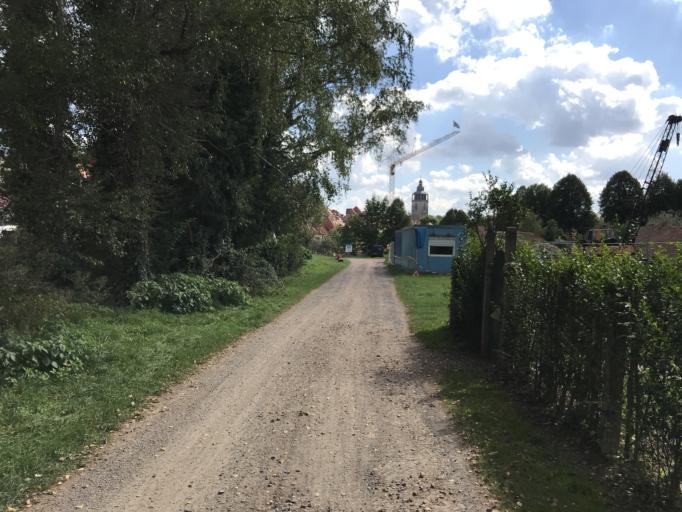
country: DE
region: Hesse
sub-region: Regierungsbezirk Kassel
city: Bad Sooden-Allendorf
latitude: 51.2736
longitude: 9.9703
